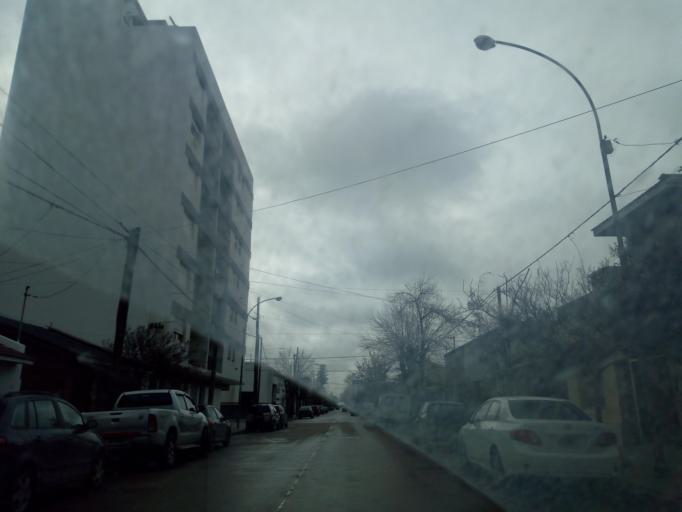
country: AR
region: Buenos Aires
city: Necochea
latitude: -38.5597
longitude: -58.7358
